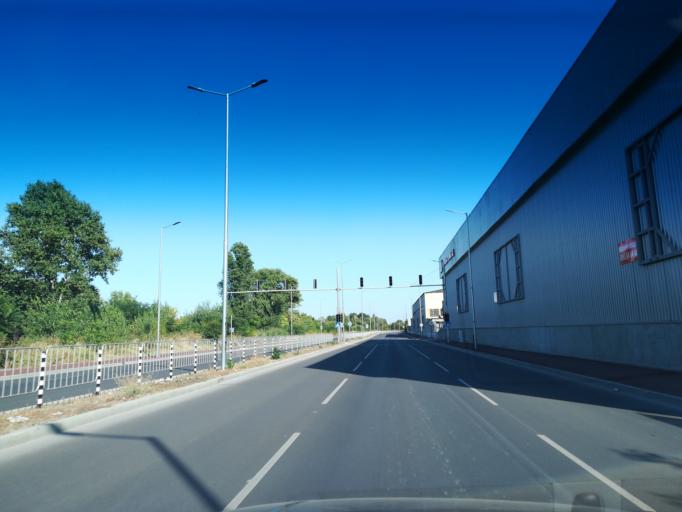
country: BG
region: Plovdiv
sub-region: Obshtina Plovdiv
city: Plovdiv
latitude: 42.1649
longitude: 24.7583
